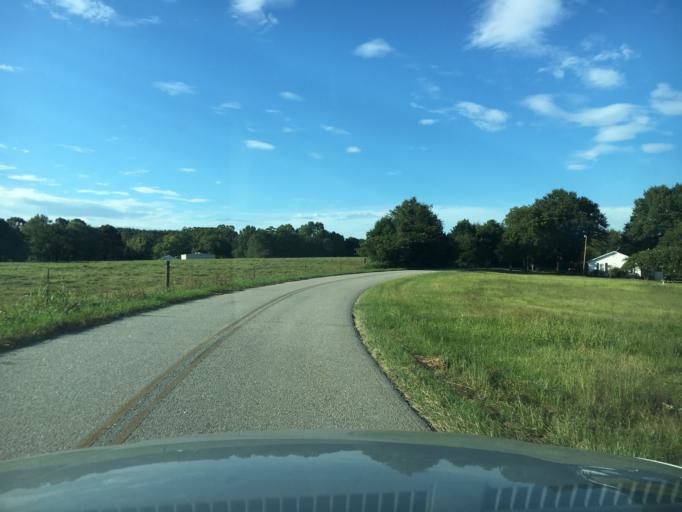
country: US
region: South Carolina
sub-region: Spartanburg County
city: Woodruff
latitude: 34.8139
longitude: -82.1048
